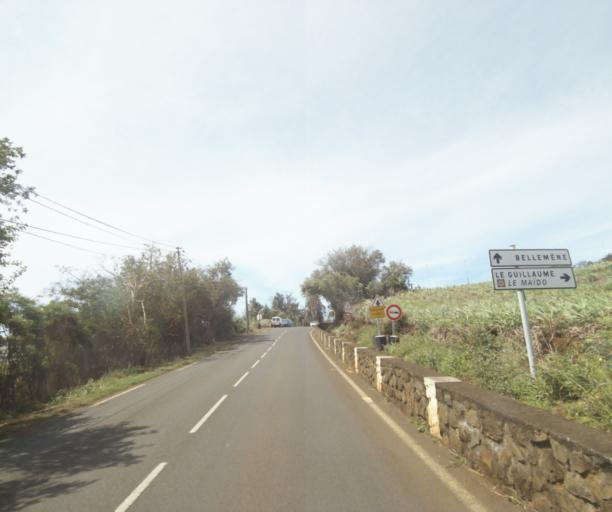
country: RE
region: Reunion
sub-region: Reunion
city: Saint-Paul
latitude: -21.0392
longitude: 55.2881
